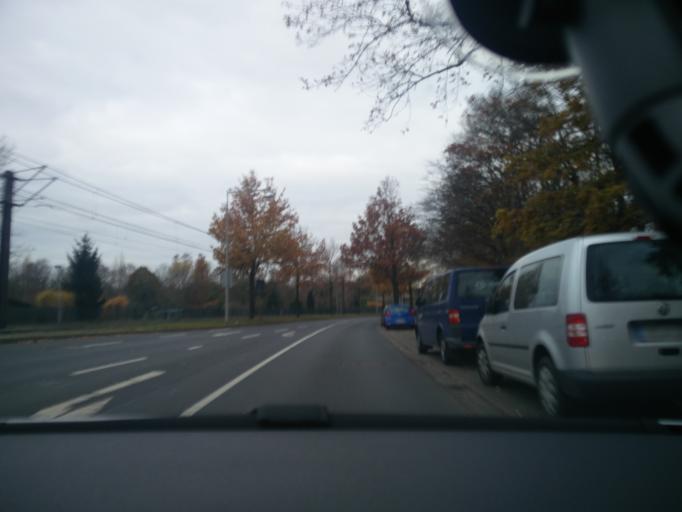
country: DE
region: Lower Saxony
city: Laatzen
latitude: 52.3548
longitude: 9.7956
